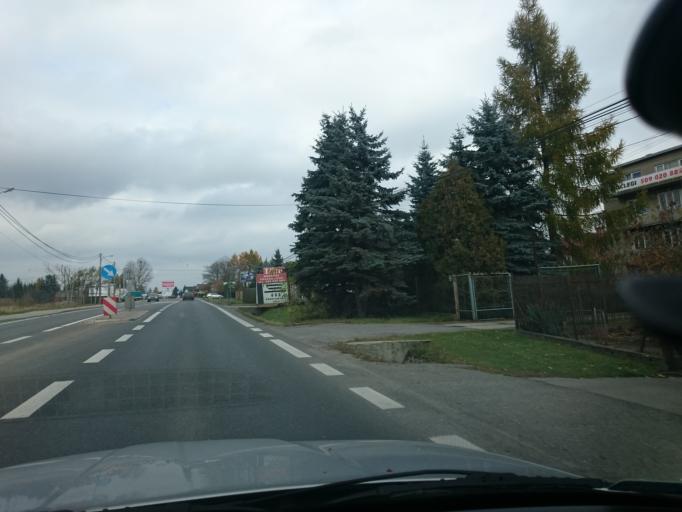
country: PL
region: Lesser Poland Voivodeship
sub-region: Powiat krakowski
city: Michalowice
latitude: 50.1272
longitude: 19.9682
